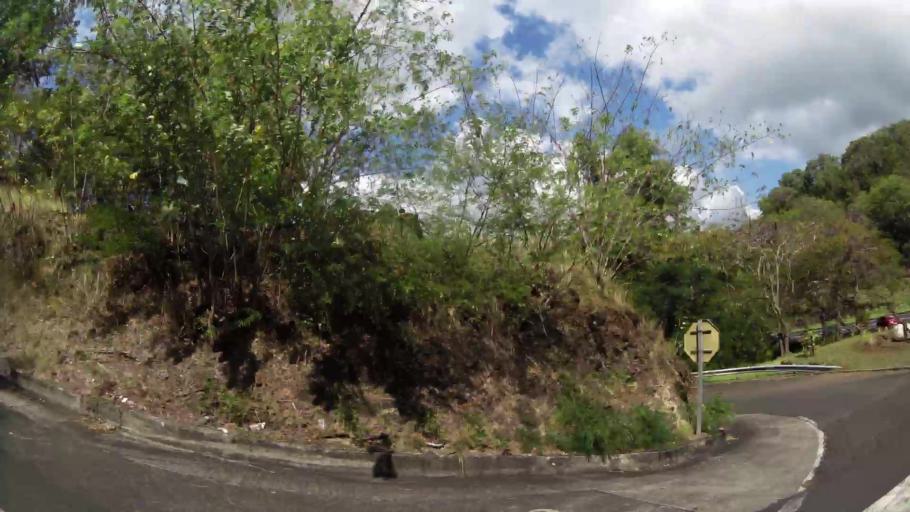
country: MQ
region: Martinique
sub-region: Martinique
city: Fort-de-France
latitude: 14.6405
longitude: -61.1360
